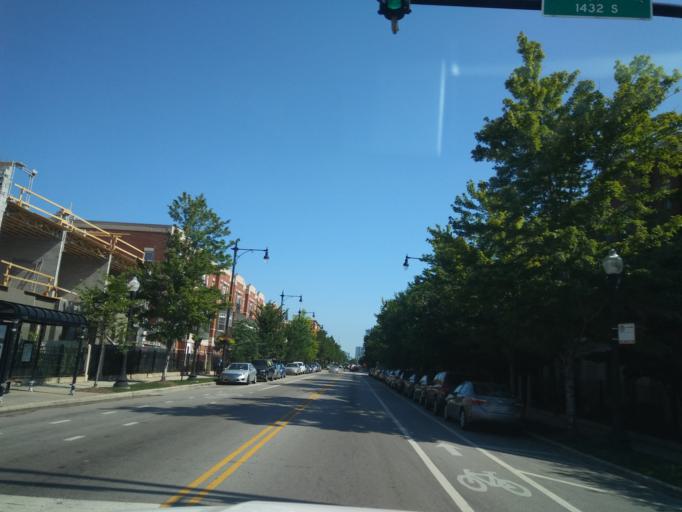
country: US
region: Illinois
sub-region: Cook County
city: Chicago
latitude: 41.8623
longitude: -87.6468
